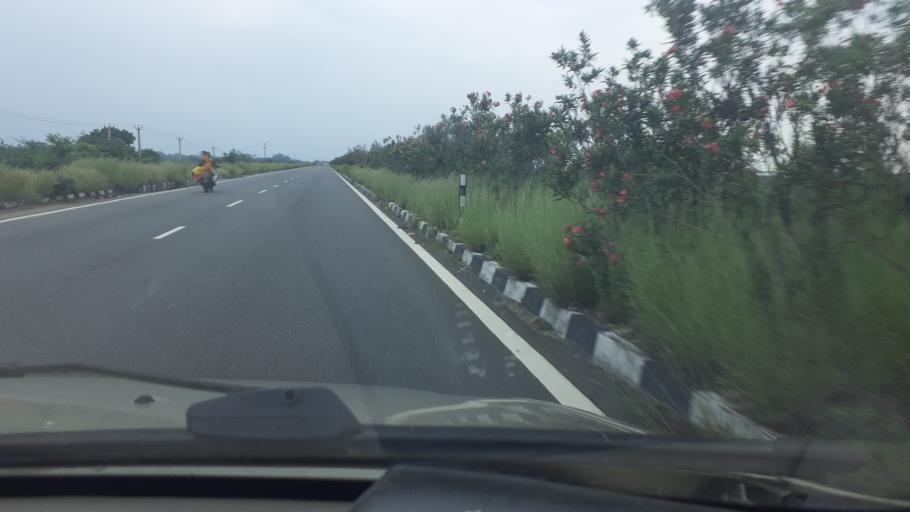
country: IN
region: Tamil Nadu
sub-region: Madurai
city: Tirupparangunram
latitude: 9.8221
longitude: 77.9771
